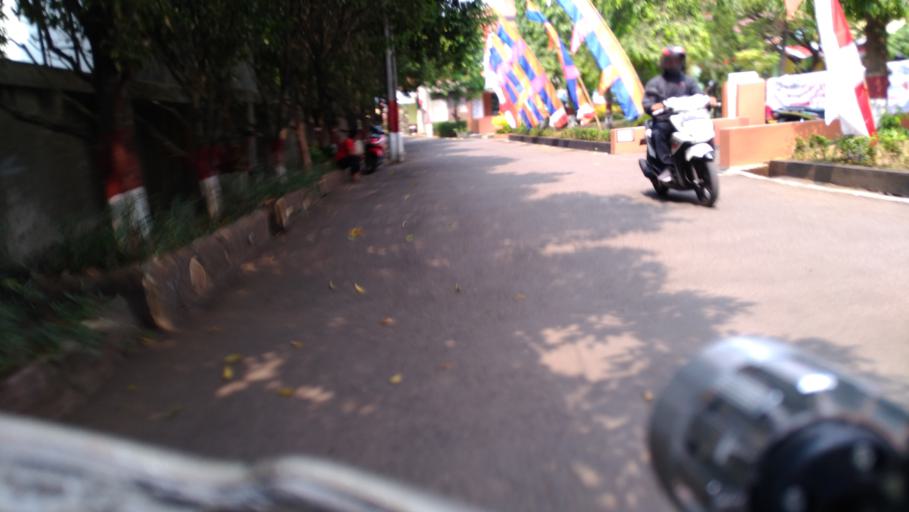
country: ID
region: West Java
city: Cileungsir
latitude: -6.3194
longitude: 106.8993
